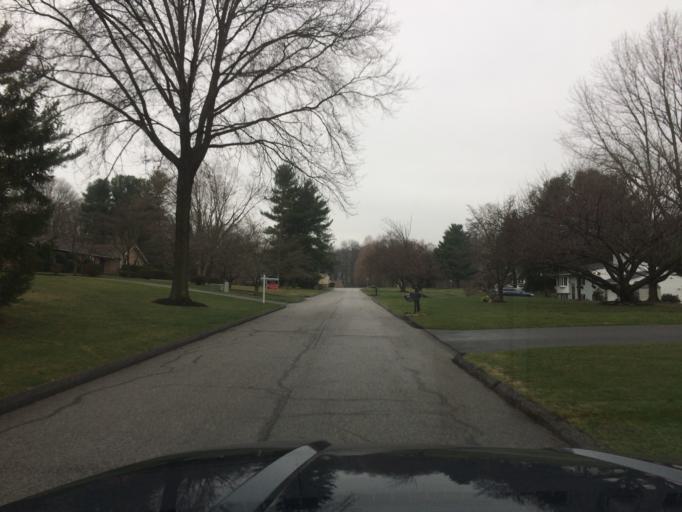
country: US
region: Maryland
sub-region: Carroll County
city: Sykesville
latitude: 39.2826
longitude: -77.0012
